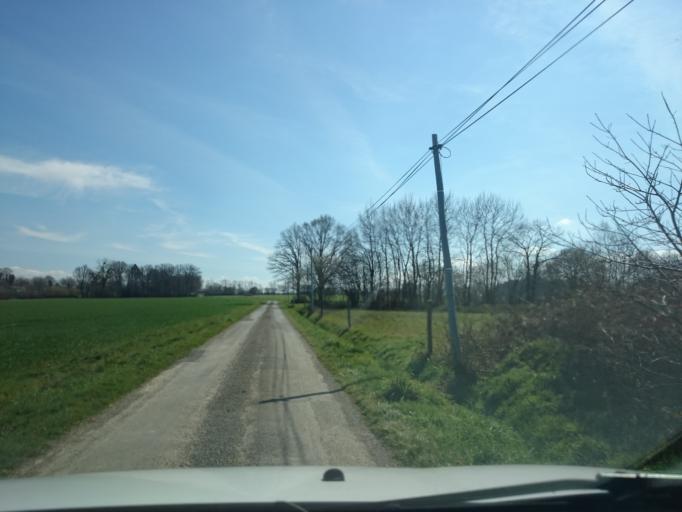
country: FR
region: Brittany
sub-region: Departement d'Ille-et-Vilaine
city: Acigne
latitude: 48.1618
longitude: -1.4962
